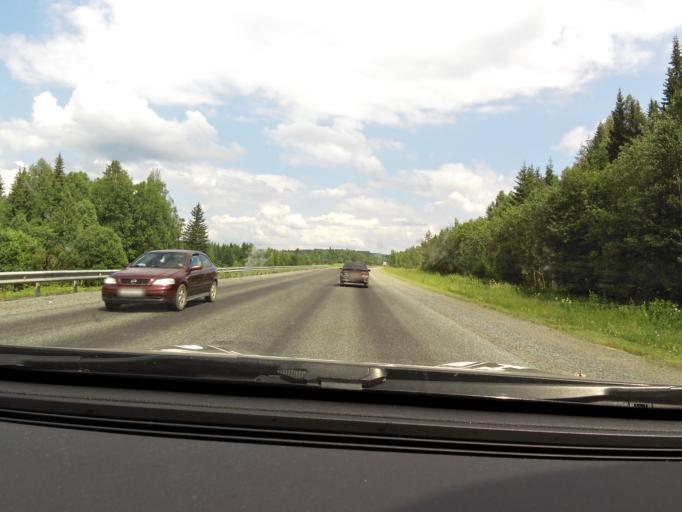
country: RU
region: Sverdlovsk
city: Arti
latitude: 56.7946
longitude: 58.4635
